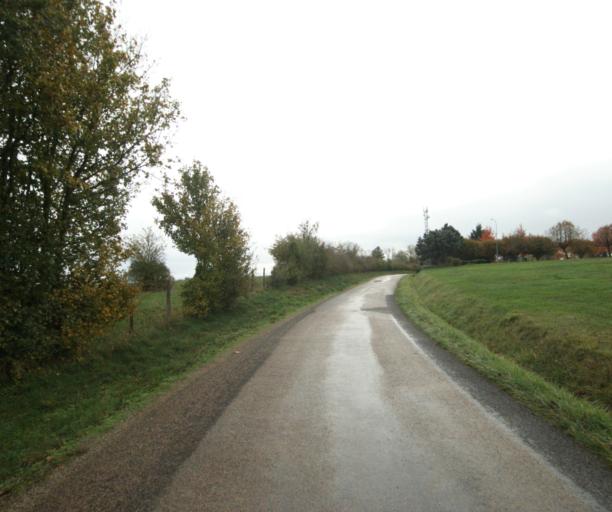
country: FR
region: Rhone-Alpes
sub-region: Departement de l'Ain
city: Pont-de-Vaux
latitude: 46.4786
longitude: 4.8740
